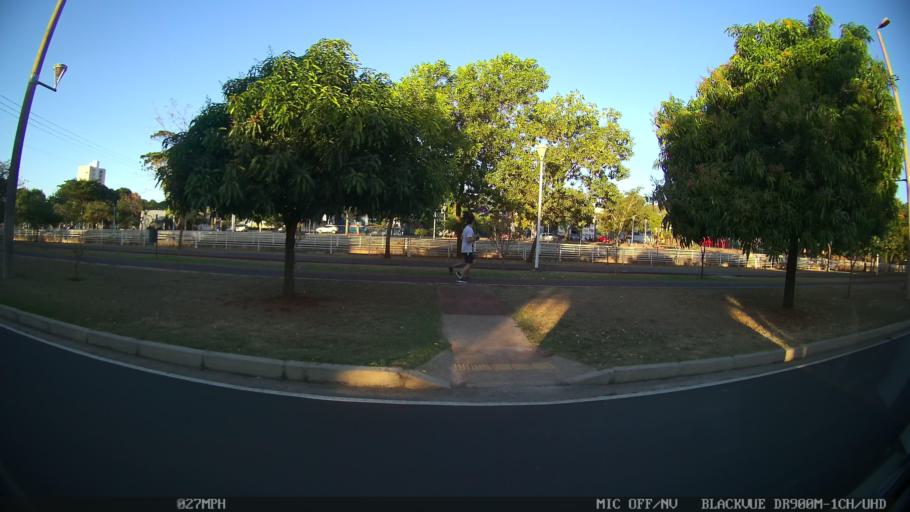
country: BR
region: Sao Paulo
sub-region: Sao Jose Do Rio Preto
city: Sao Jose do Rio Preto
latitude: -20.7885
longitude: -49.3770
